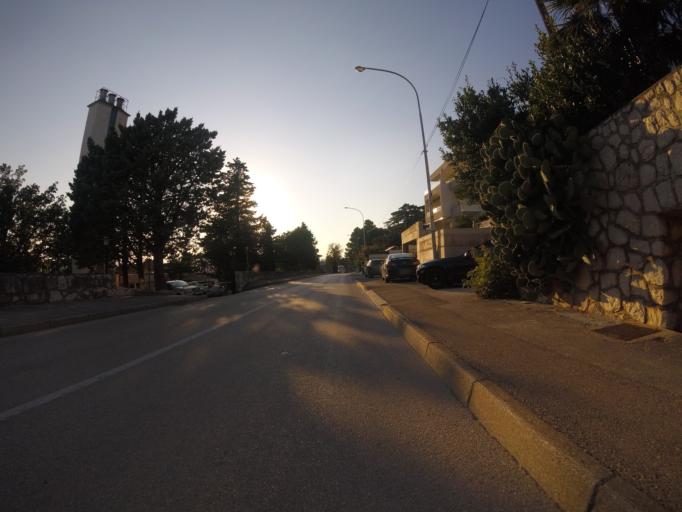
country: HR
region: Primorsko-Goranska
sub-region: Grad Crikvenica
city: Crikvenica
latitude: 45.1864
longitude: 14.6776
